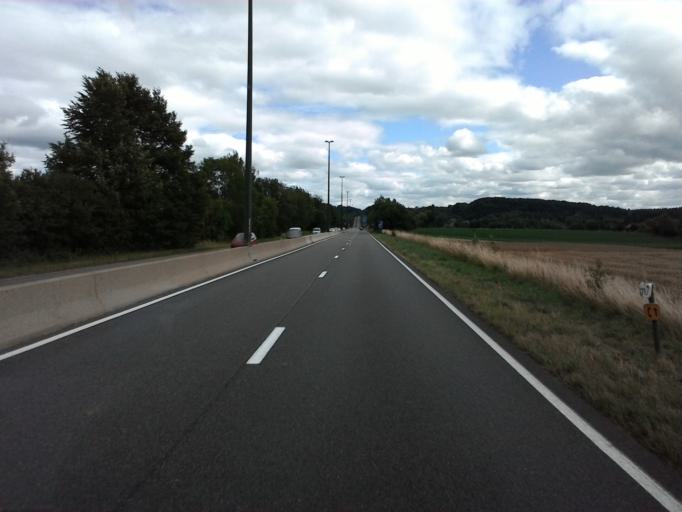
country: BE
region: Wallonia
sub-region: Province du Luxembourg
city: Attert
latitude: 49.7310
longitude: 5.7933
